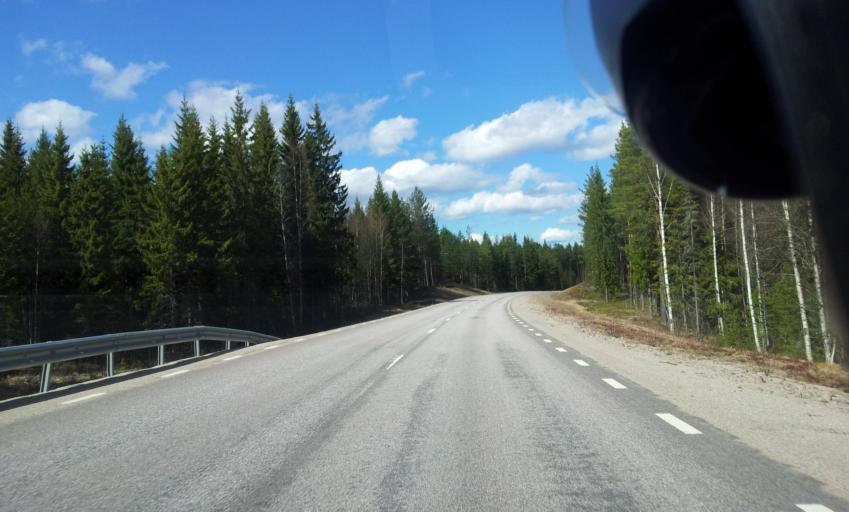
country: SE
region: Gaevleborg
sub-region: Bollnas Kommun
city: Vittsjo
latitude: 61.1572
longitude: 15.8829
